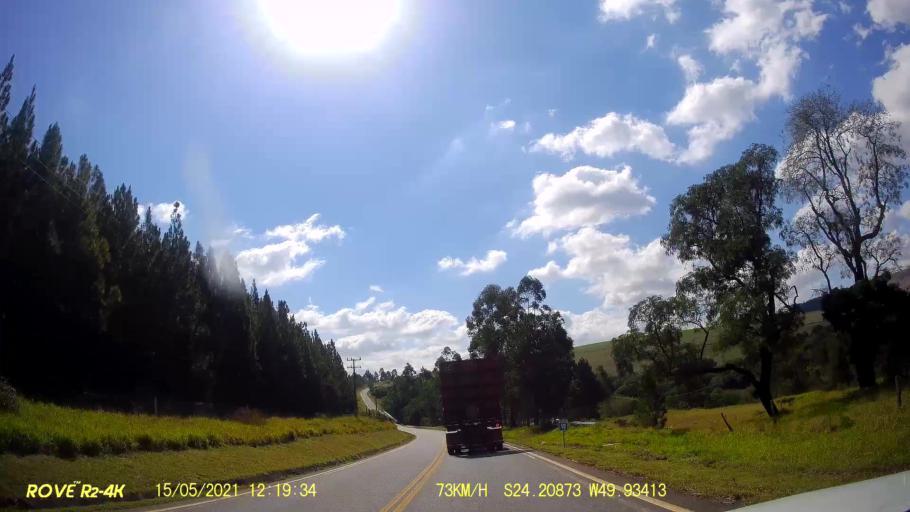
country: BR
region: Parana
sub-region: Jaguariaiva
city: Jaguariaiva
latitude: -24.2076
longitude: -49.9336
